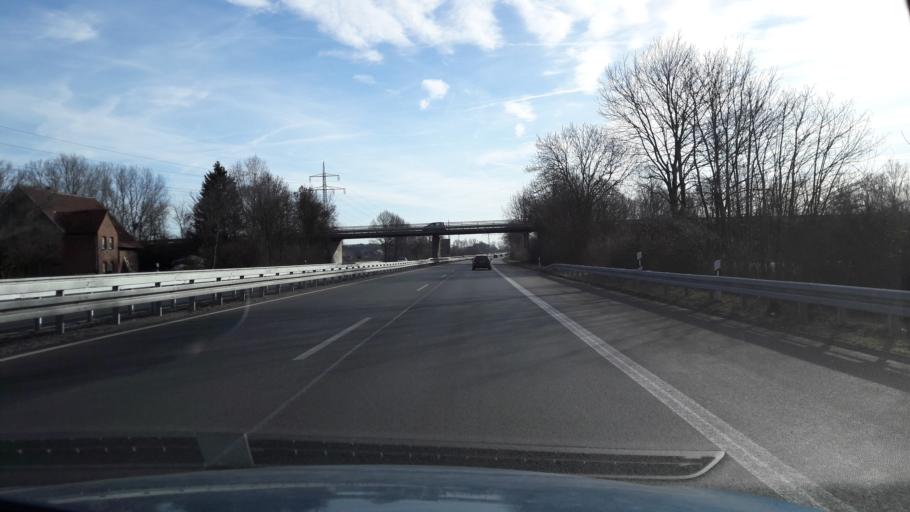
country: DE
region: North Rhine-Westphalia
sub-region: Regierungsbezirk Detmold
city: Rheda-Wiedenbruck
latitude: 51.8433
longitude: 8.3343
